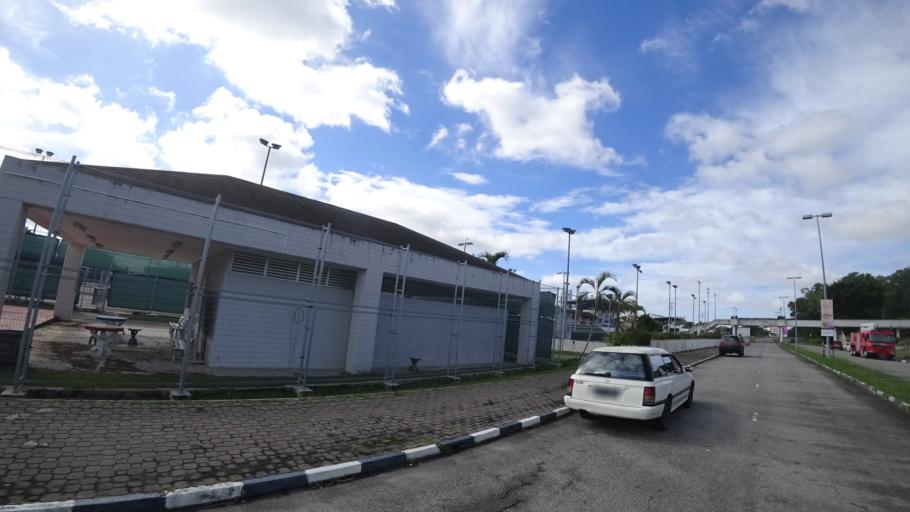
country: BN
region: Brunei and Muara
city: Bandar Seri Begawan
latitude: 4.9278
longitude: 114.9478
